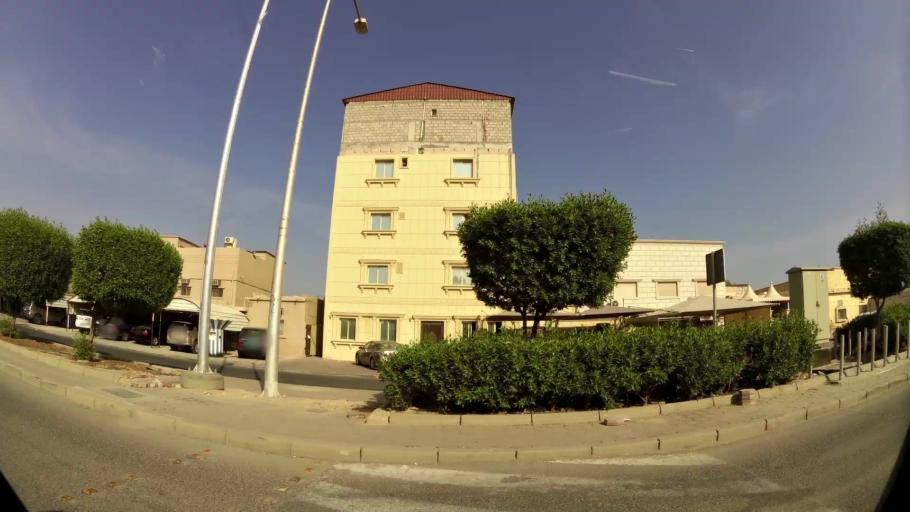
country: KW
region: Al Ahmadi
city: Ar Riqqah
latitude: 29.1378
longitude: 48.1085
